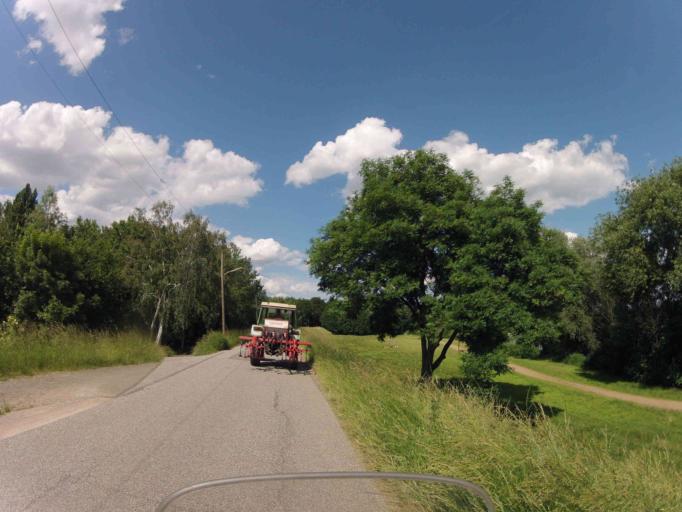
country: DE
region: Hamburg
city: Rothenburgsort
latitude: 53.4861
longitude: 10.0839
